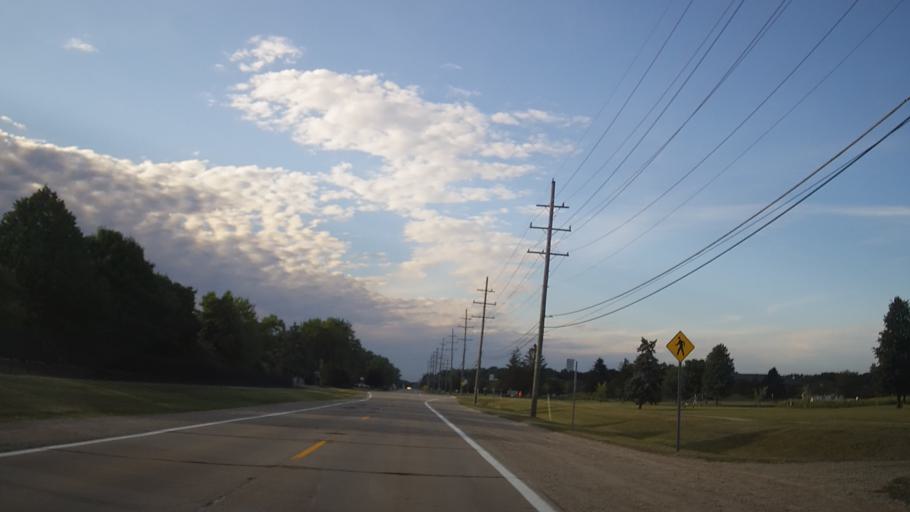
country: US
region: Michigan
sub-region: Macomb County
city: Clinton
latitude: 42.5948
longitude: -82.9320
